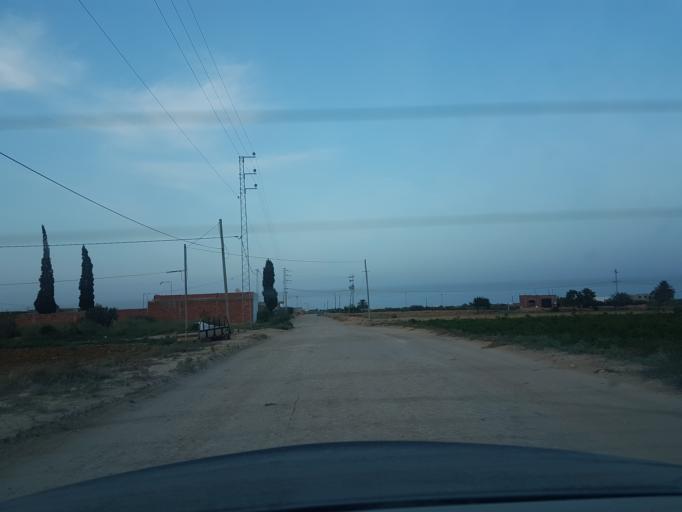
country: TN
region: Safaqis
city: Sfax
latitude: 34.7061
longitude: 10.6850
